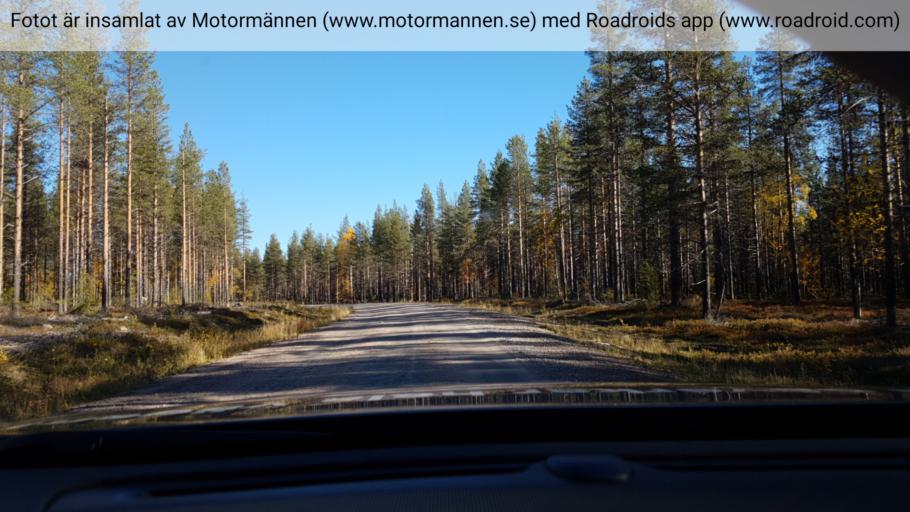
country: SE
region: Norrbotten
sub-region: Gallivare Kommun
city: Gaellivare
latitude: 66.5483
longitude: 20.9966
